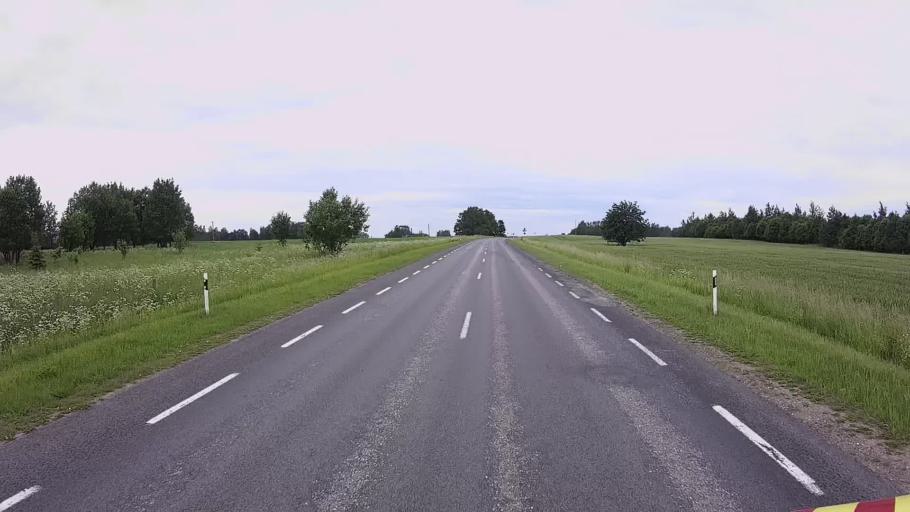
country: EE
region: Viljandimaa
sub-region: Karksi vald
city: Karksi-Nuia
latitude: 58.1813
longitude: 25.5921
